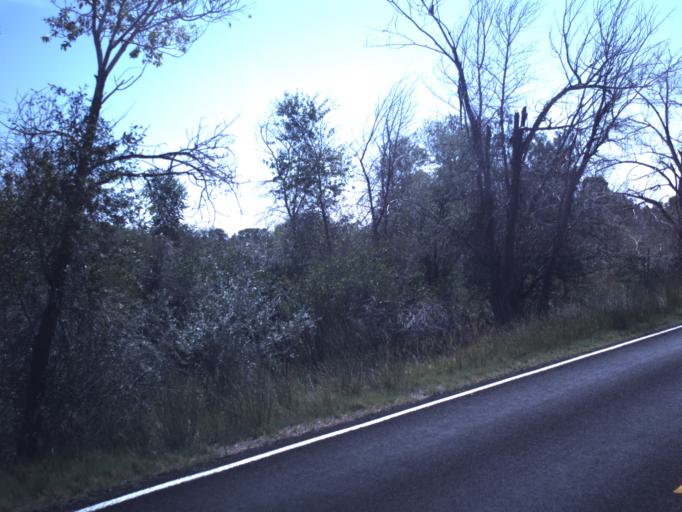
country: US
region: Utah
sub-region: Duchesne County
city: Roosevelt
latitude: 40.4251
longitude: -109.9245
